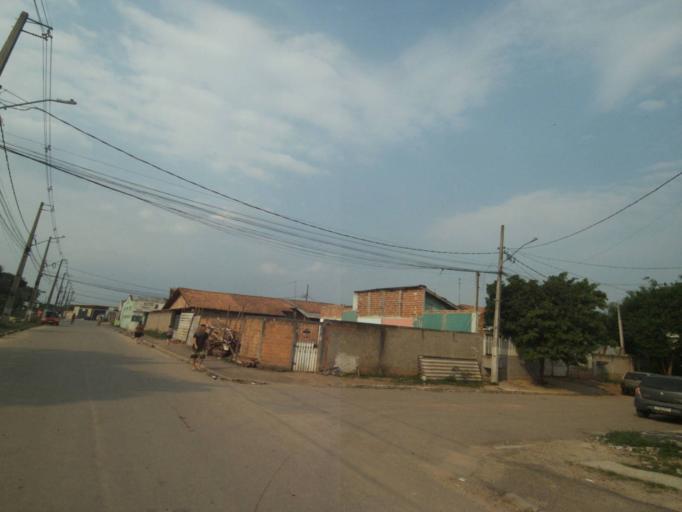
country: BR
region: Parana
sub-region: Sao Jose Dos Pinhais
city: Sao Jose dos Pinhais
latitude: -25.5341
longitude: -49.2314
